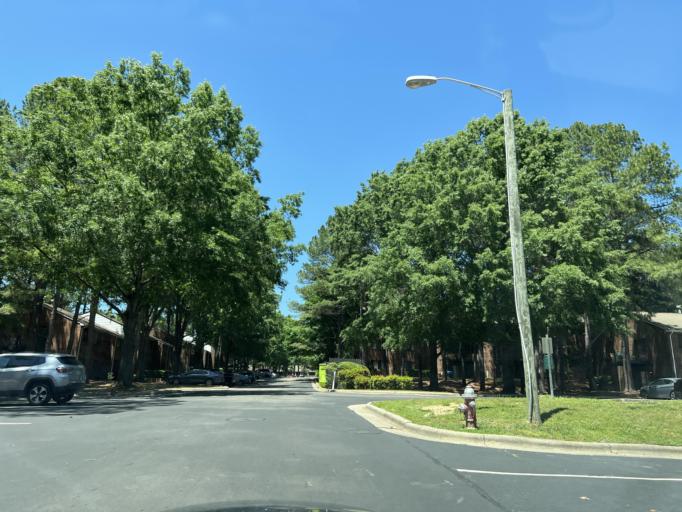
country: US
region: North Carolina
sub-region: Wake County
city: Raleigh
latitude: 35.8530
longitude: -78.5725
